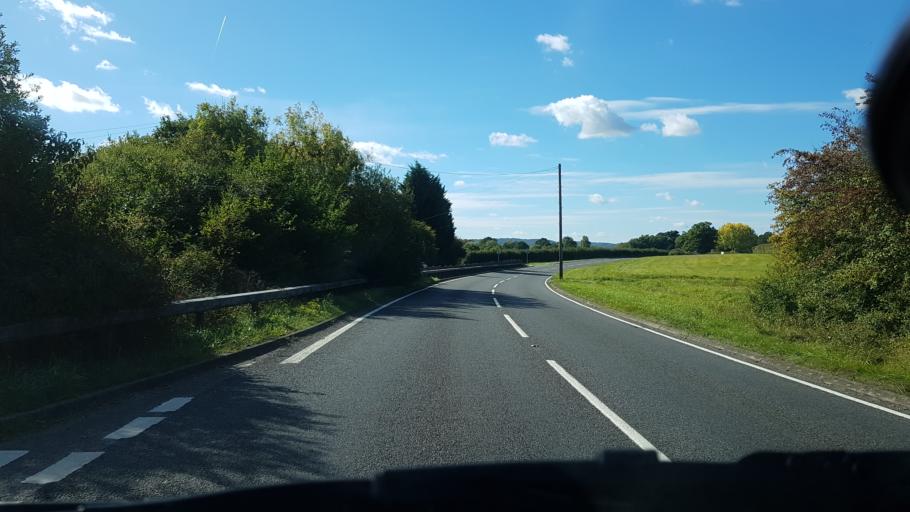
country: GB
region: England
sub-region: West Sussex
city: Billingshurst
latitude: 51.0211
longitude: -0.4657
